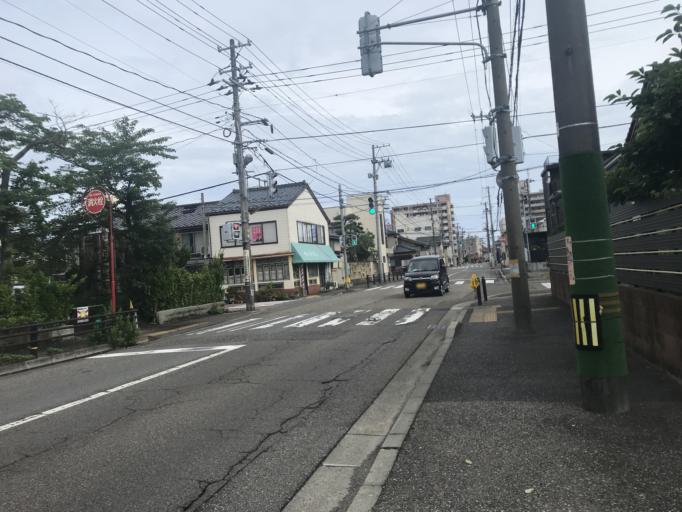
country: JP
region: Niigata
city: Niigata-shi
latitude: 37.9274
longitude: 139.0533
